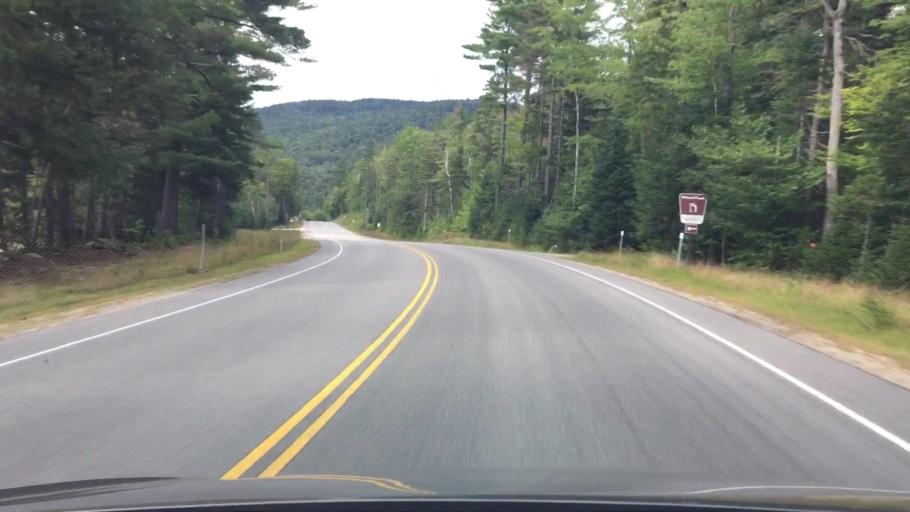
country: US
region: New Hampshire
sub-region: Carroll County
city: Tamworth
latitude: 43.9997
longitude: -71.2769
